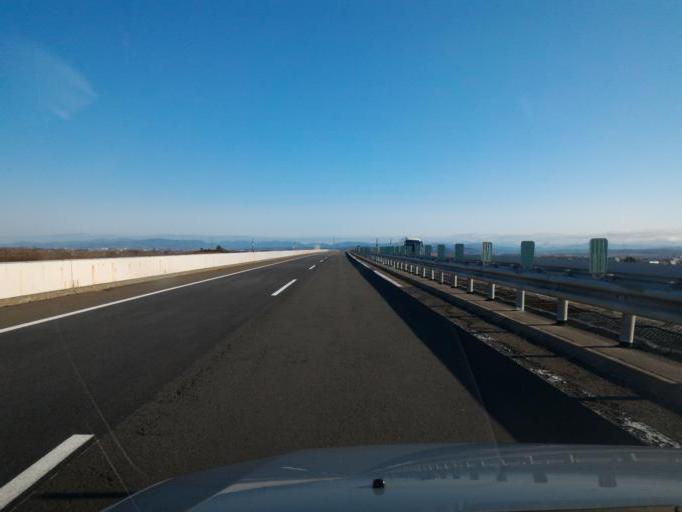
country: JP
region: Hokkaido
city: Iwamizawa
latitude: 43.1473
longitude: 141.6896
